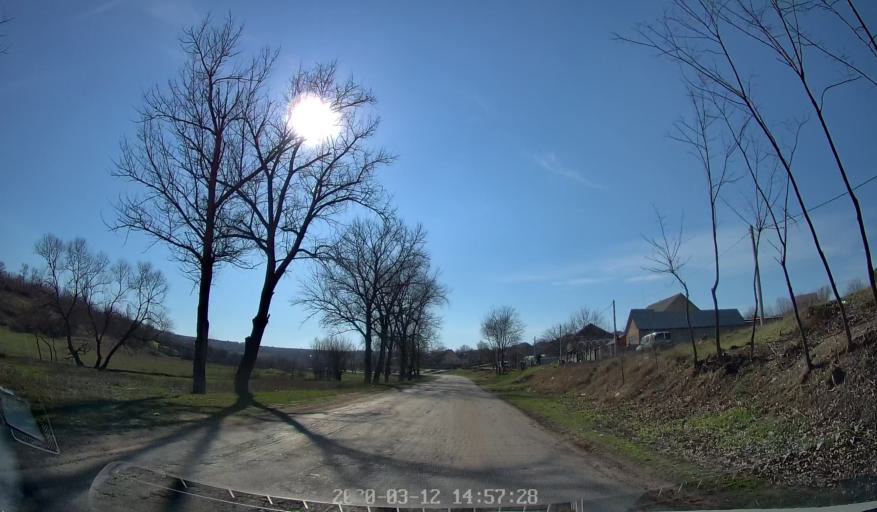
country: MD
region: Telenesti
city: Cocieri
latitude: 47.2235
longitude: 29.0379
